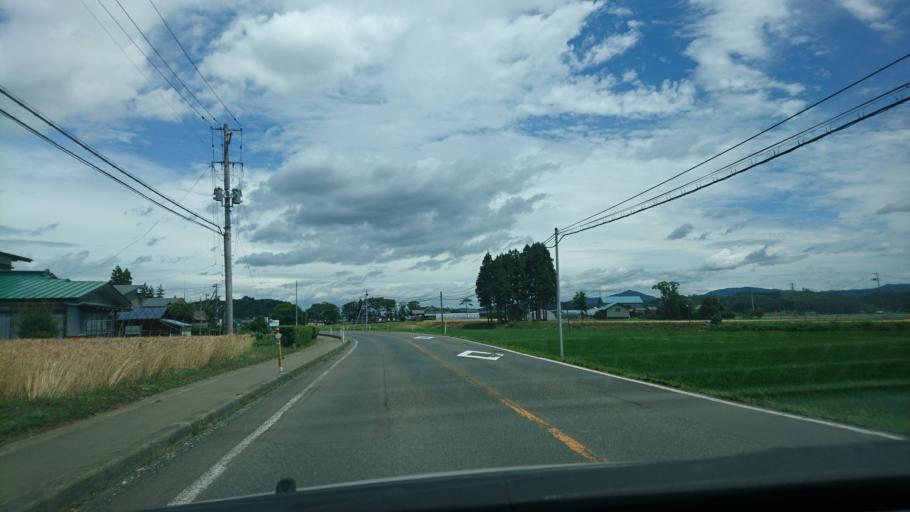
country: JP
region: Iwate
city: Morioka-shi
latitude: 39.5465
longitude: 141.1790
